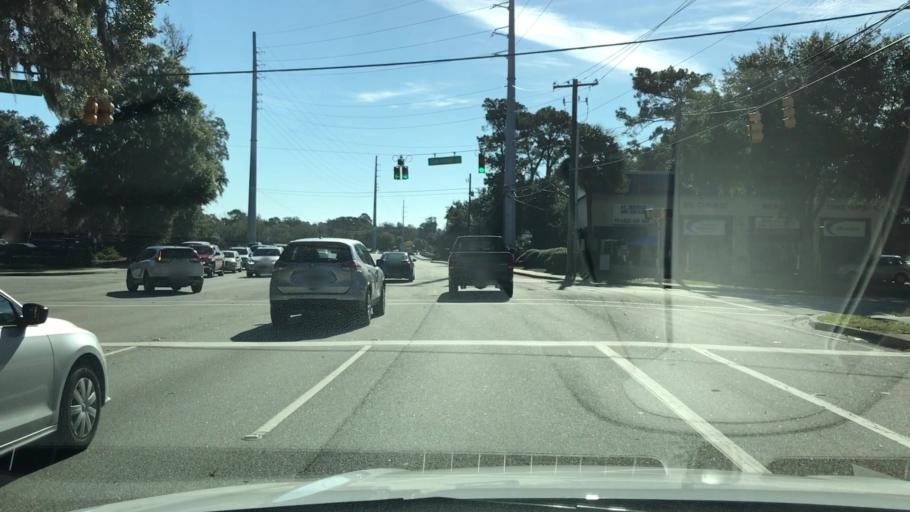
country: US
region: South Carolina
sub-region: Charleston County
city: Charleston
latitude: 32.7464
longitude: -79.9707
